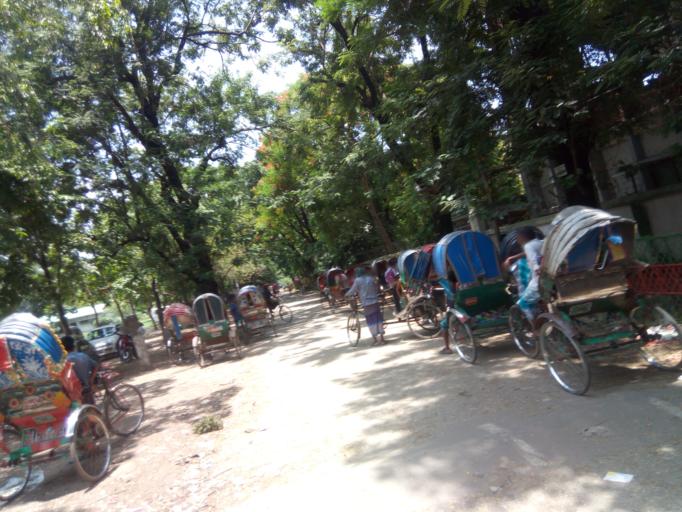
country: BD
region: Dhaka
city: Azimpur
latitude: 23.7332
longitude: 90.3895
